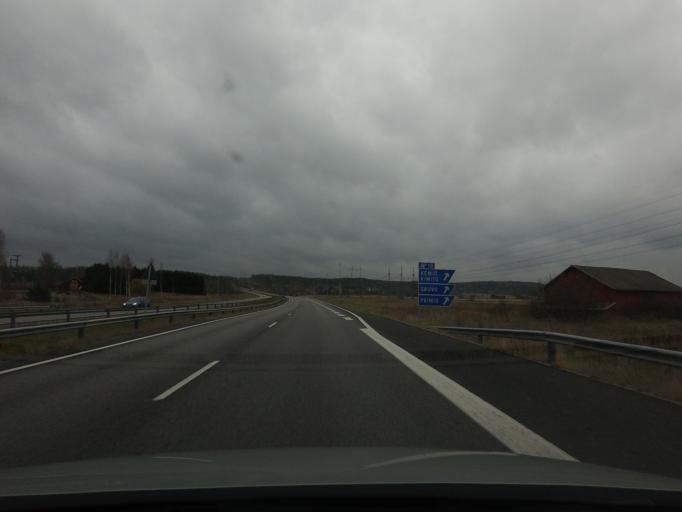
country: FI
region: Varsinais-Suomi
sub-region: Turku
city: Paimio
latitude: 60.4281
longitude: 22.6602
